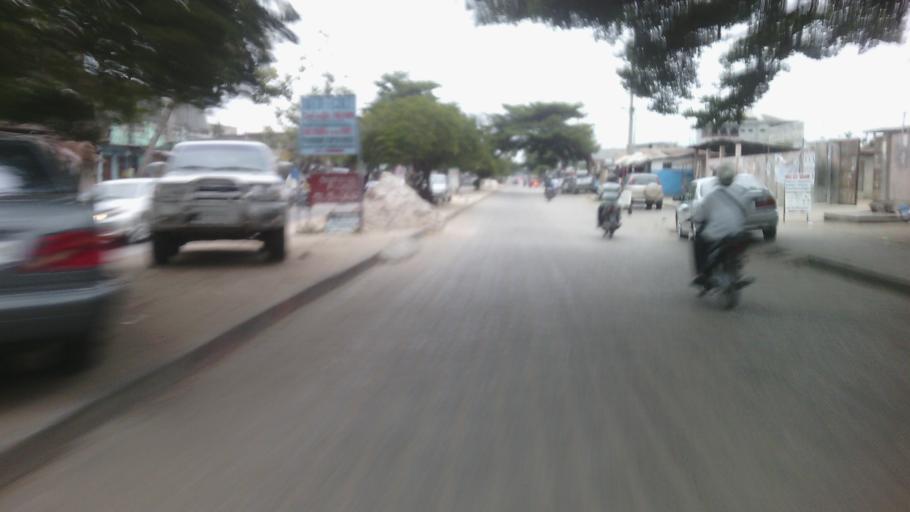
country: BJ
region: Atlantique
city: Abomey-Calavi
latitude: 6.3924
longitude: 2.3612
